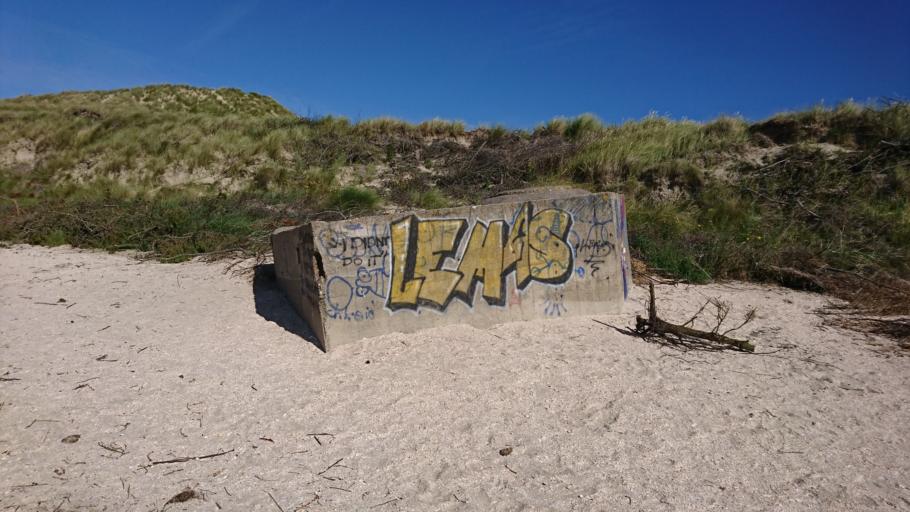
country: DK
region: South Denmark
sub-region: Fano Kommune
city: Nordby
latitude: 55.3395
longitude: 8.4673
